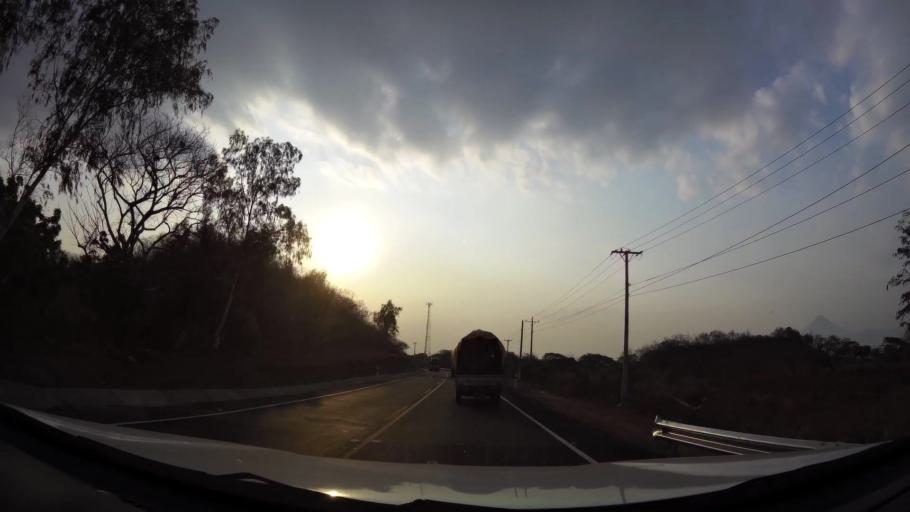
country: NI
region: Leon
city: Nagarote
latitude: 12.2760
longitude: -86.4970
